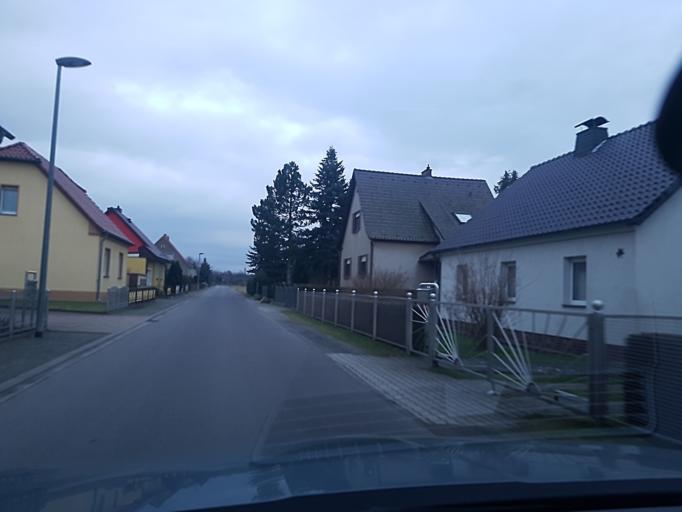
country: DE
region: Brandenburg
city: Doberlug-Kirchhain
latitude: 51.6092
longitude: 13.5588
